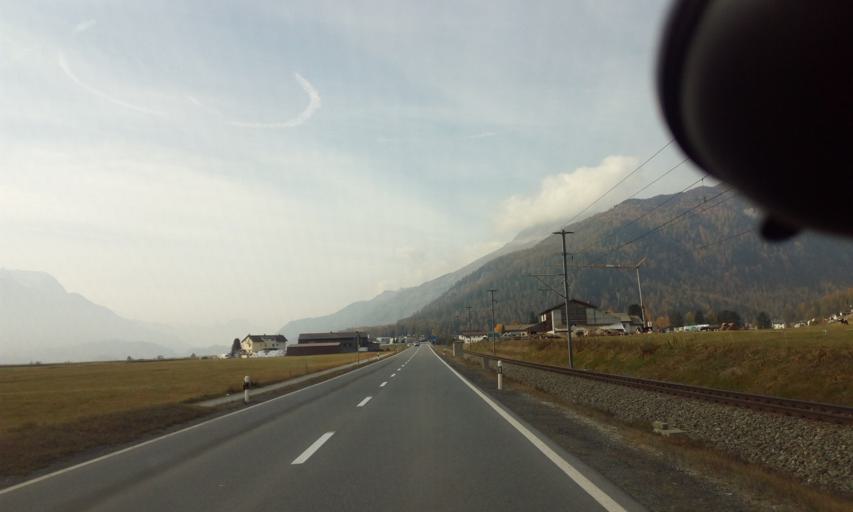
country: CH
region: Grisons
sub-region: Maloja District
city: Ponte
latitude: 46.5559
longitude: 9.8978
